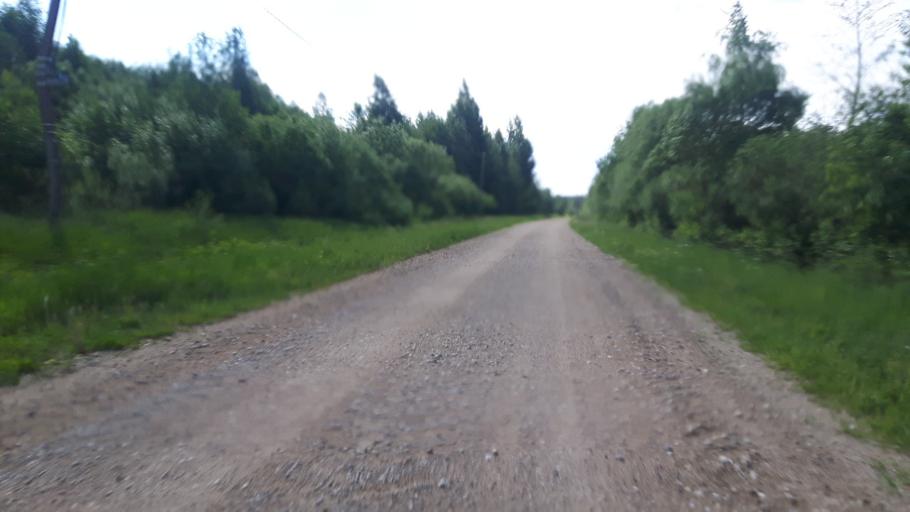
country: EE
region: Paernumaa
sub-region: Vaendra vald (alev)
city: Vandra
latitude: 58.7011
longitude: 25.0291
